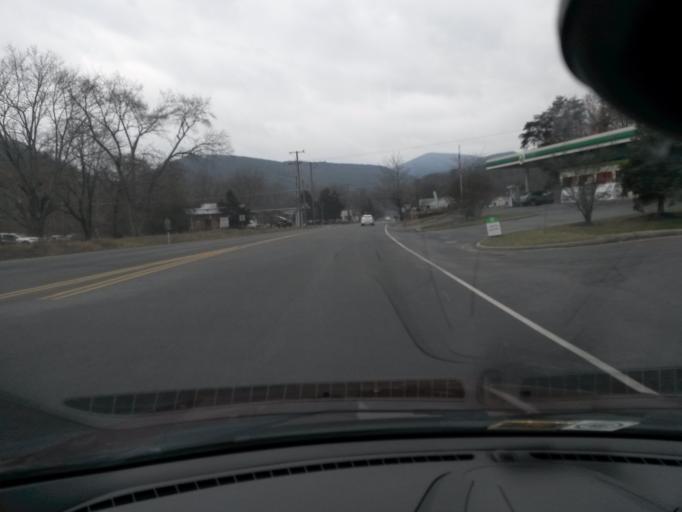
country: US
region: Virginia
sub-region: Alleghany County
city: Clifton Forge
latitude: 37.8256
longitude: -79.7938
